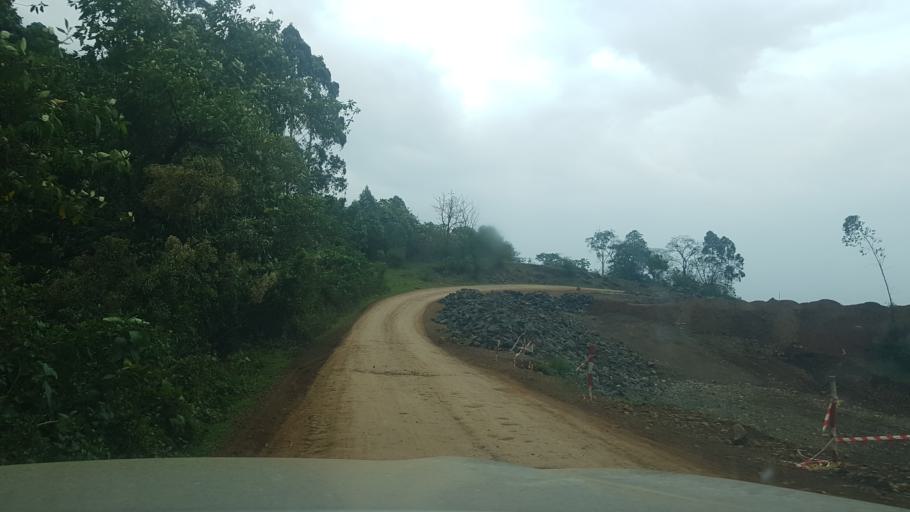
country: ET
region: Oromiya
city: Gore
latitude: 7.9195
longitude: 35.5146
